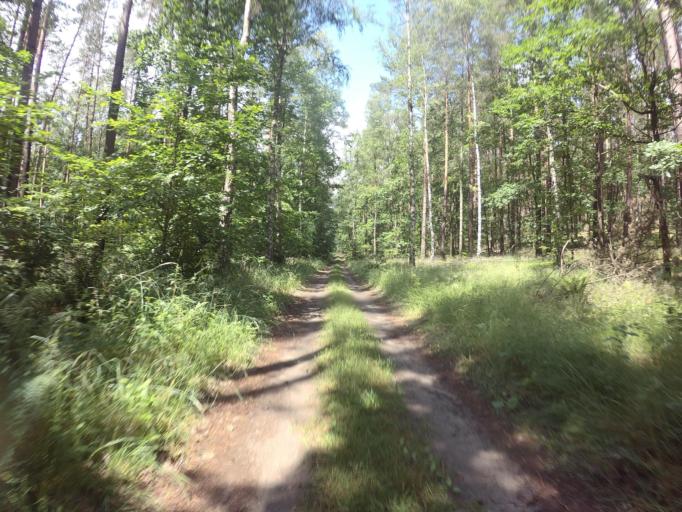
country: PL
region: West Pomeranian Voivodeship
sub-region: Powiat choszczenski
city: Bierzwnik
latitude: 53.0268
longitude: 15.5772
